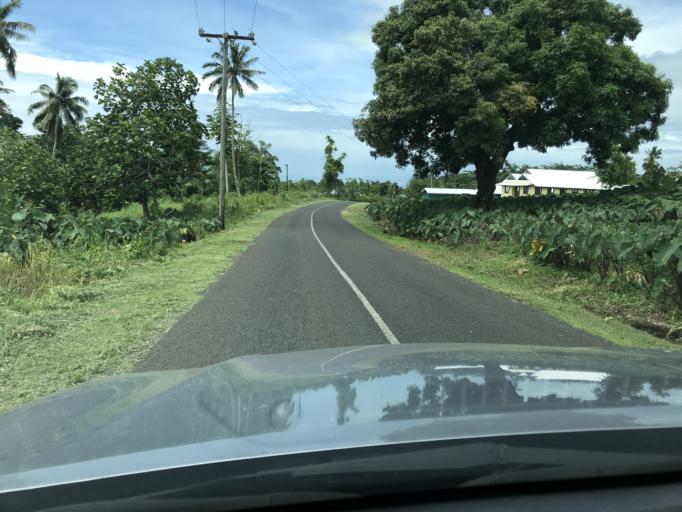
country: WS
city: Fasito`outa
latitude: -13.8659
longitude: -171.9121
